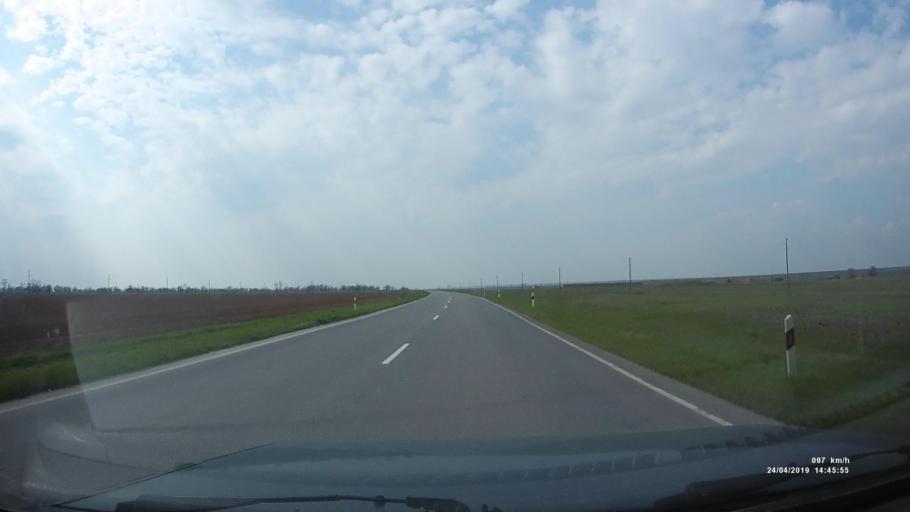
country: RU
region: Rostov
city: Remontnoye
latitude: 46.4771
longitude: 43.7988
